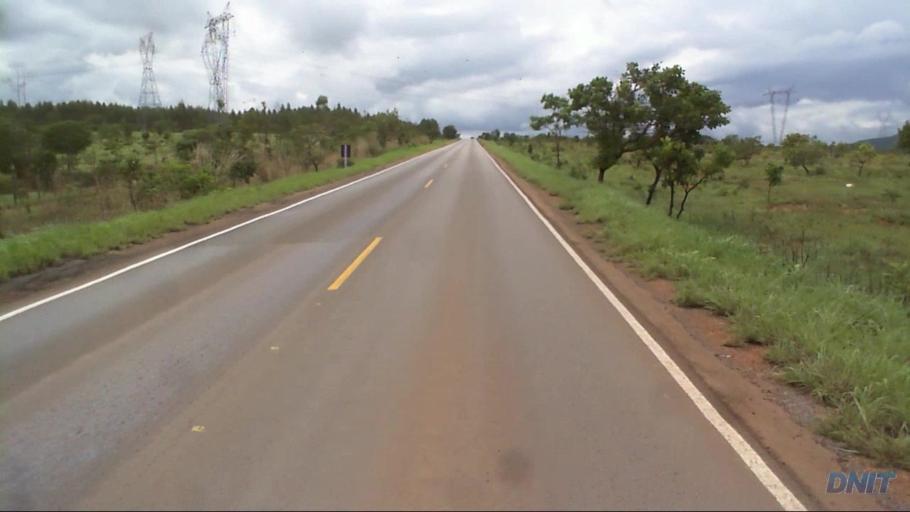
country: BR
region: Goias
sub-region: Padre Bernardo
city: Padre Bernardo
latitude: -15.3769
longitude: -48.2147
